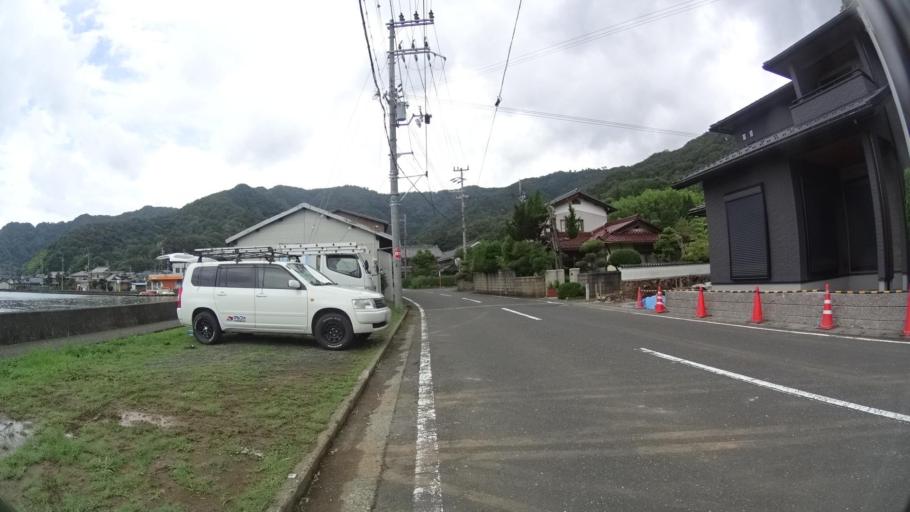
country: JP
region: Kyoto
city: Maizuru
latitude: 35.5100
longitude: 135.3741
